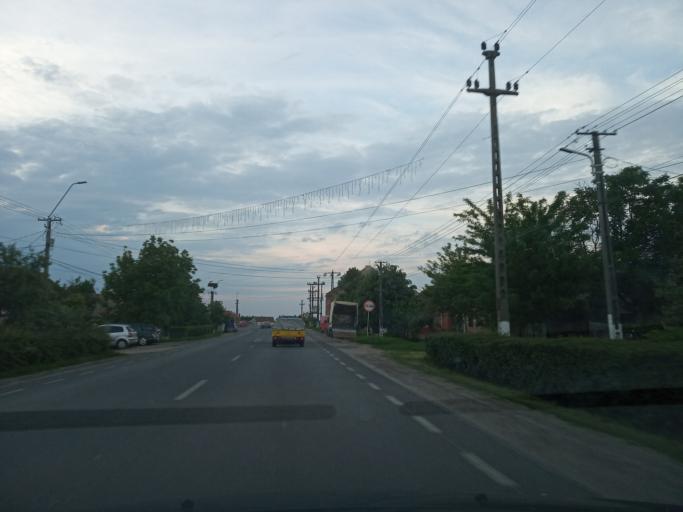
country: RO
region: Timis
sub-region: Comuna Denta
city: Denta
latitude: 45.3633
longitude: 21.2478
